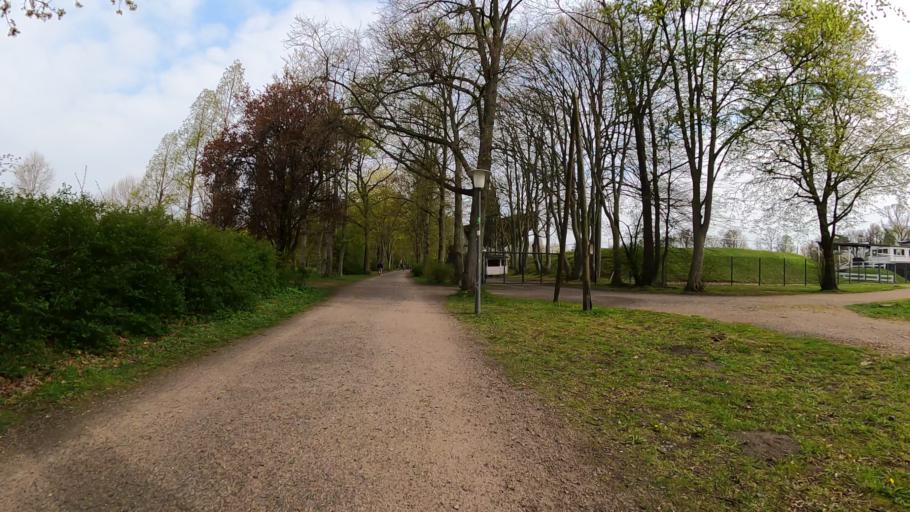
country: DE
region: Hamburg
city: Eidelstedt
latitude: 53.5551
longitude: 9.8612
